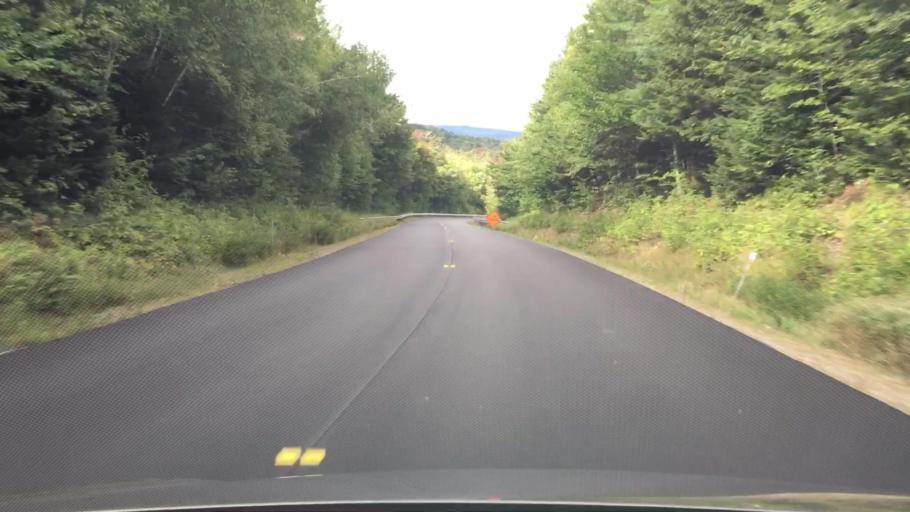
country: US
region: New Hampshire
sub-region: Carroll County
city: Sandwich
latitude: 44.0185
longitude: -71.4506
